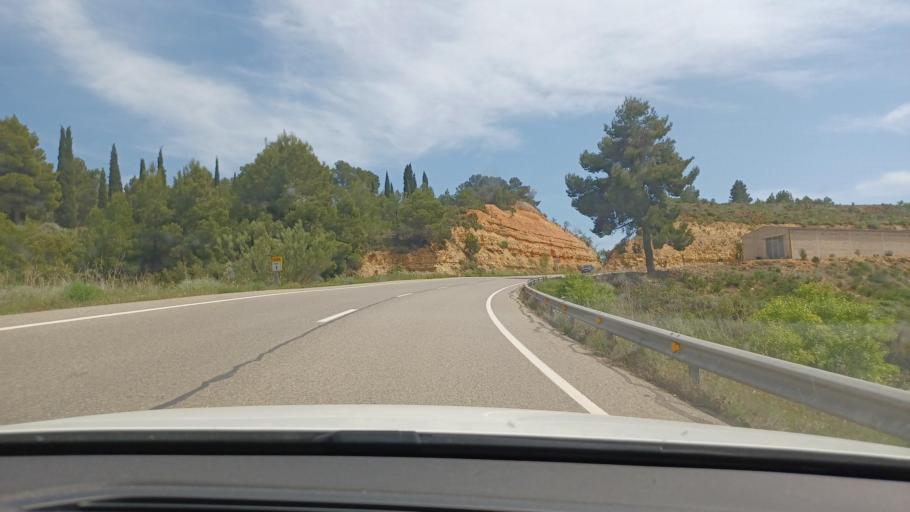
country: ES
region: Catalonia
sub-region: Provincia de Tarragona
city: Gandesa
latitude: 41.0619
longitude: 0.4371
